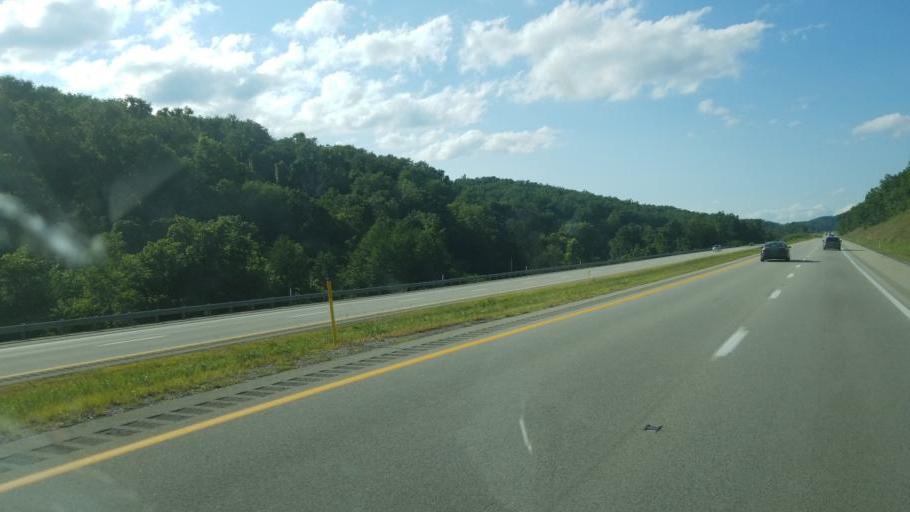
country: US
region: Pennsylvania
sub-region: Greene County
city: Waynesburg
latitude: 39.9710
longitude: -80.1757
